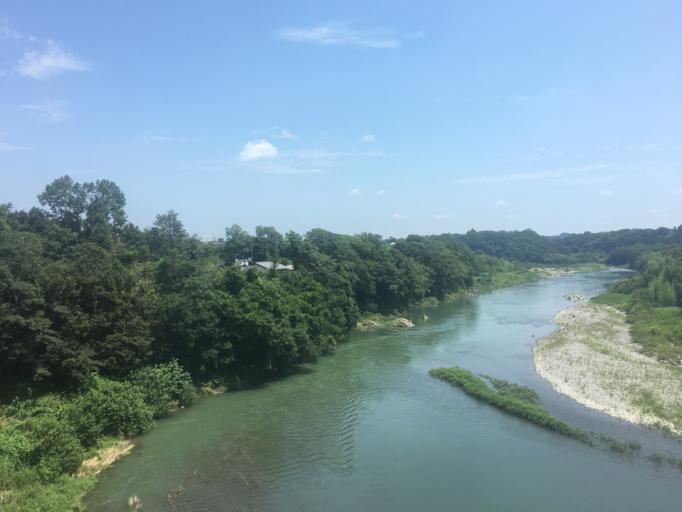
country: JP
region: Saitama
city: Yorii
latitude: 36.1132
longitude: 139.1845
